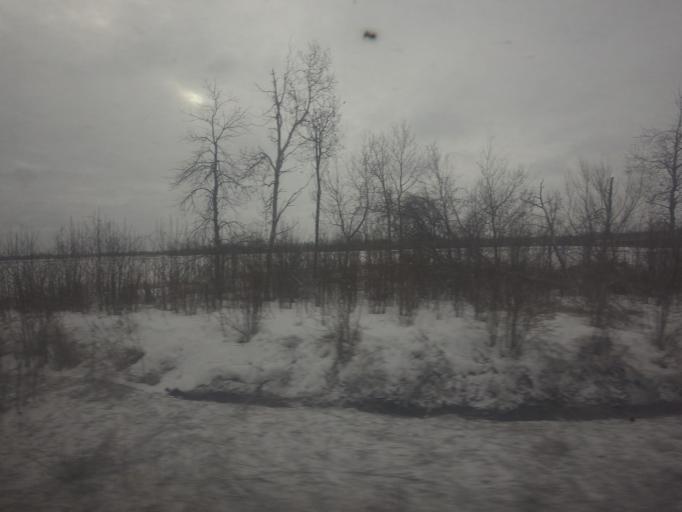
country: CA
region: Ontario
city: Bells Corners
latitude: 45.2548
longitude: -75.7831
